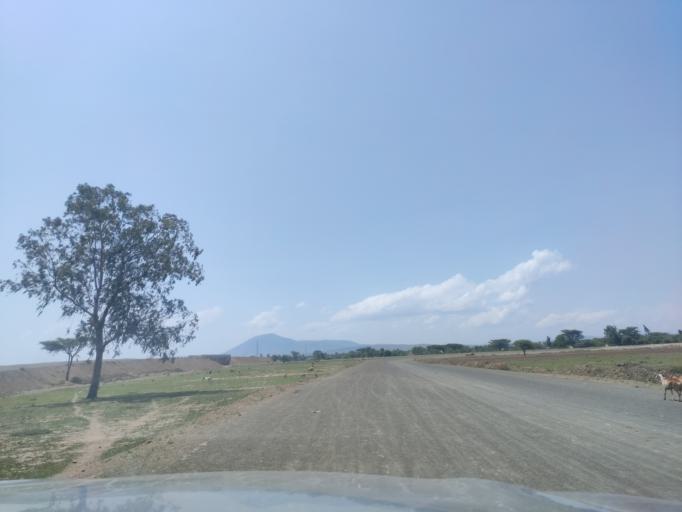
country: ET
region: Oromiya
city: Mojo
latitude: 8.3026
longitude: 38.9325
